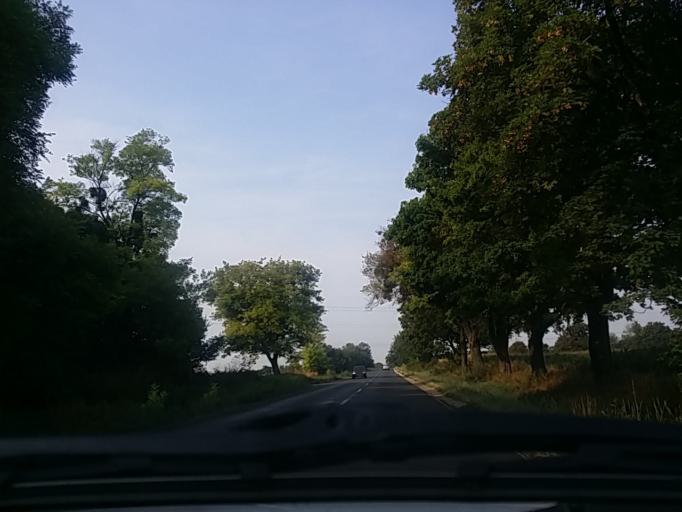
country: HU
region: Fejer
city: Csakvar
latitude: 47.4036
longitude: 18.4825
